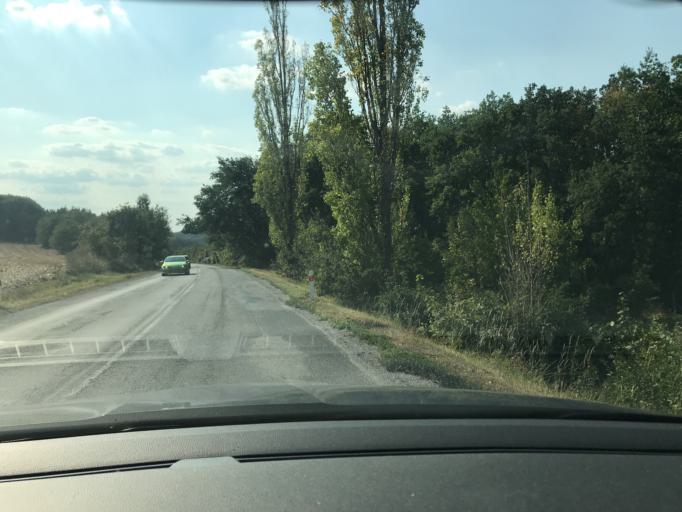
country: CZ
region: Central Bohemia
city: Kralupy nad Vltavou
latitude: 50.2170
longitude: 14.3157
